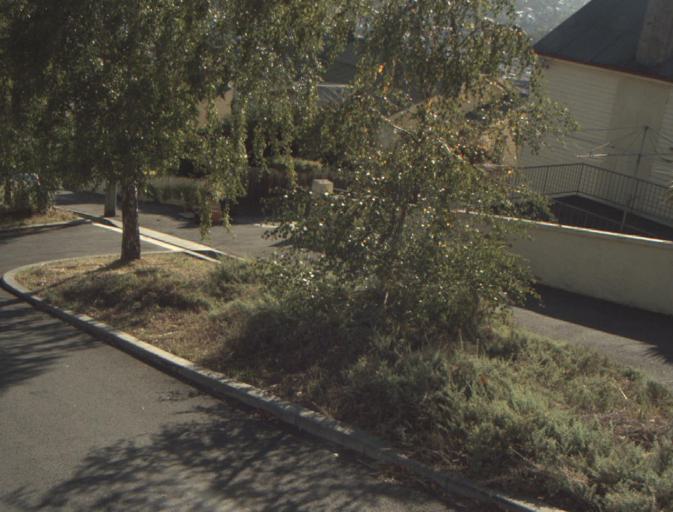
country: AU
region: Tasmania
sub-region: Launceston
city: East Launceston
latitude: -41.4428
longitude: 147.1456
